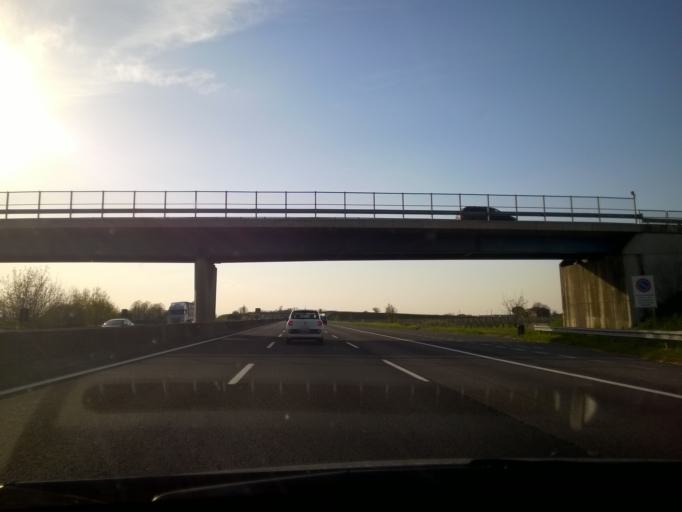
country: IT
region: Emilia-Romagna
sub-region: Provincia di Bologna
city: Imola
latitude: 44.3907
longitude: 11.7142
